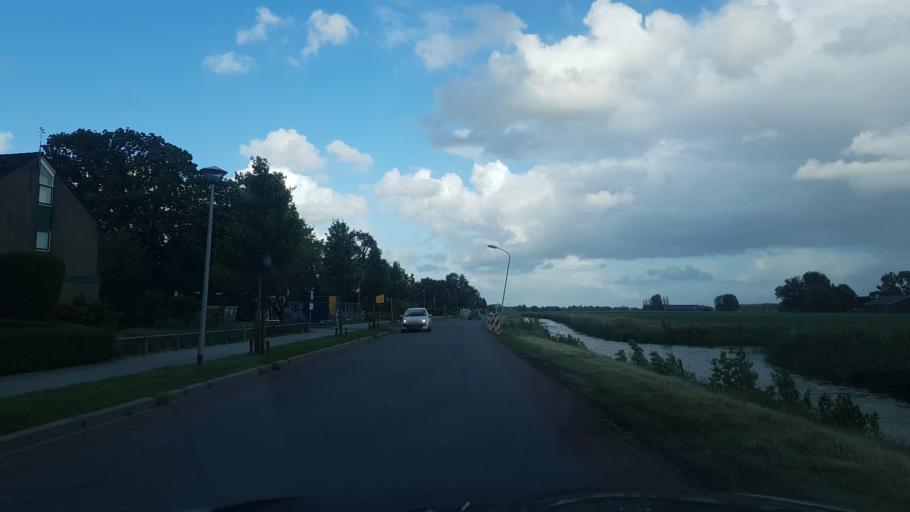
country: NL
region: Groningen
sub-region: Gemeente Appingedam
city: Appingedam
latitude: 53.3284
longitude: 6.7464
